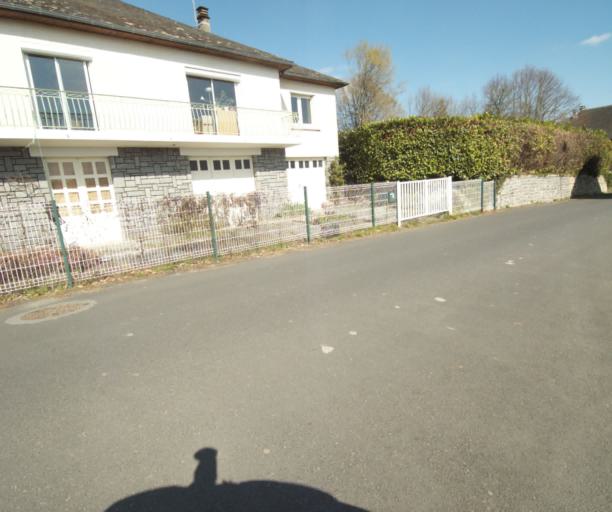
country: FR
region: Limousin
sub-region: Departement de la Correze
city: Saint-Mexant
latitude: 45.3097
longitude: 1.6381
